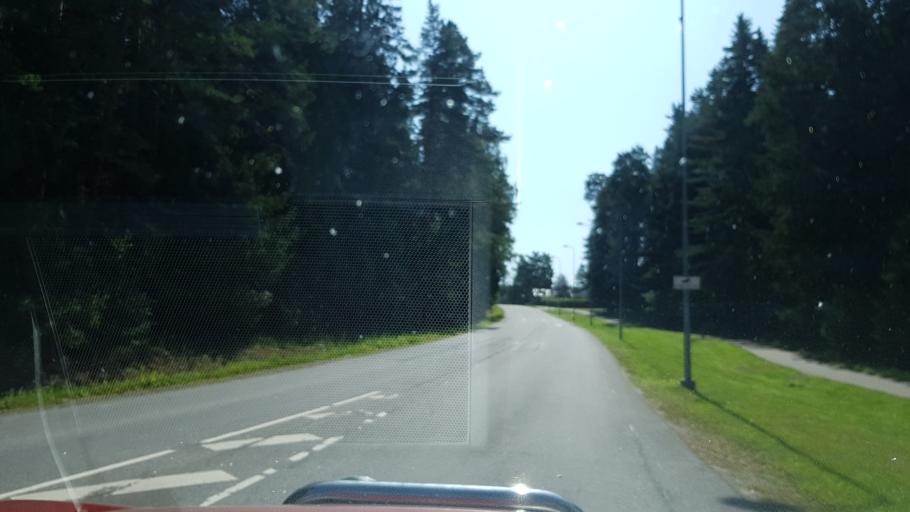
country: EE
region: Vorumaa
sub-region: Voru linn
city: Voru
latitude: 57.7376
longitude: 27.2780
